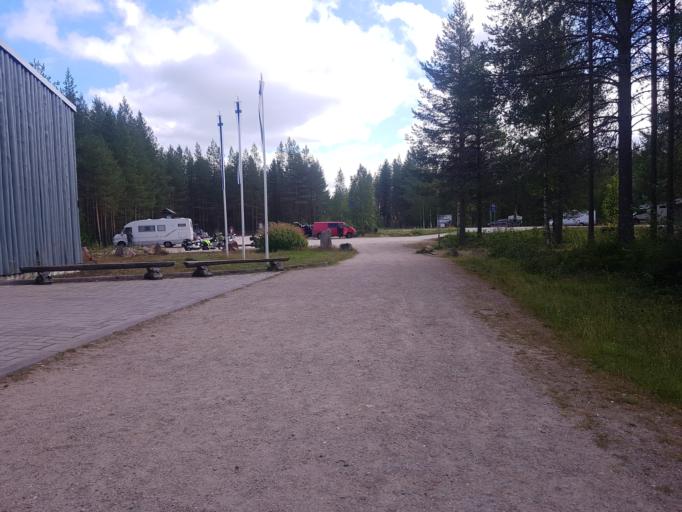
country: FI
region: Kainuu
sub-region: Kehys-Kainuu
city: Suomussalmi
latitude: 64.8482
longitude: 29.3266
